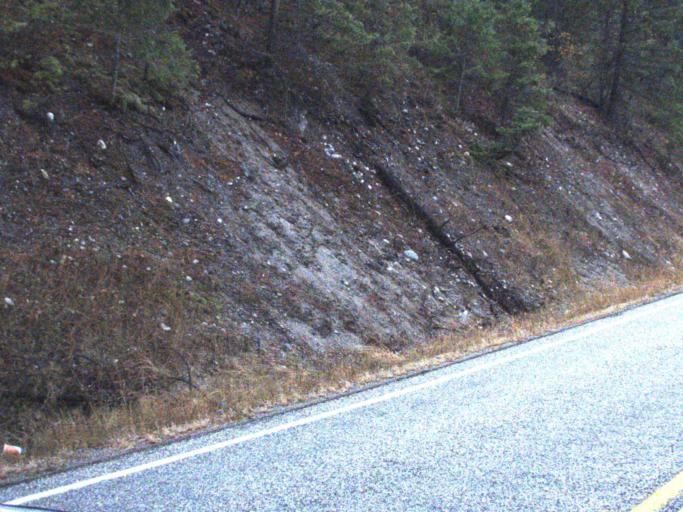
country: US
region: Washington
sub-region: Stevens County
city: Kettle Falls
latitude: 48.7881
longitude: -118.1512
